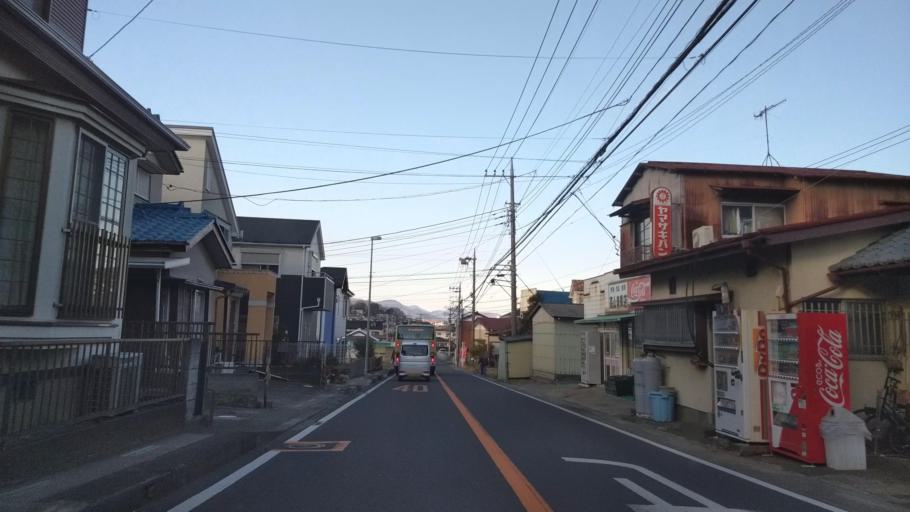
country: JP
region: Kanagawa
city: Isehara
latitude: 35.3481
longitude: 139.3029
